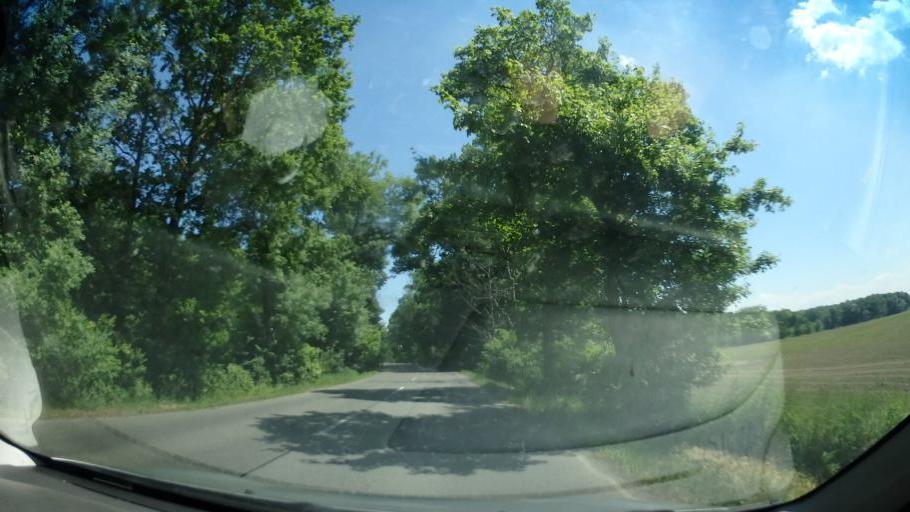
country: CZ
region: Zlin
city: Chropyne
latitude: 49.3503
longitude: 17.3382
